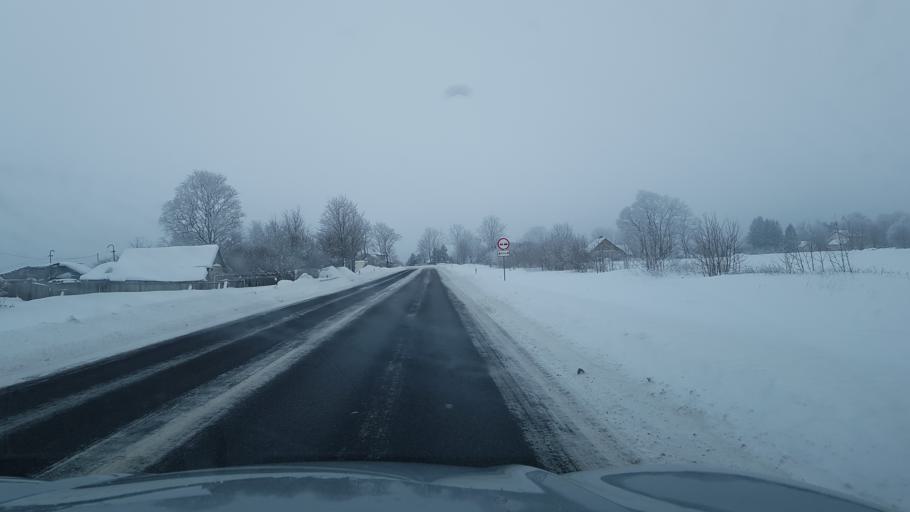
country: EE
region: Ida-Virumaa
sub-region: Johvi vald
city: Johvi
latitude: 59.3203
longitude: 27.3956
